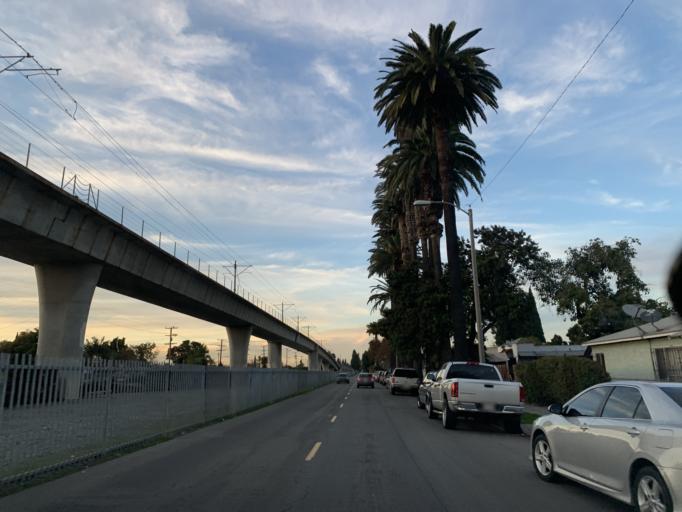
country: US
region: California
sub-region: Los Angeles County
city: Compton
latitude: 33.9049
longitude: -118.2253
